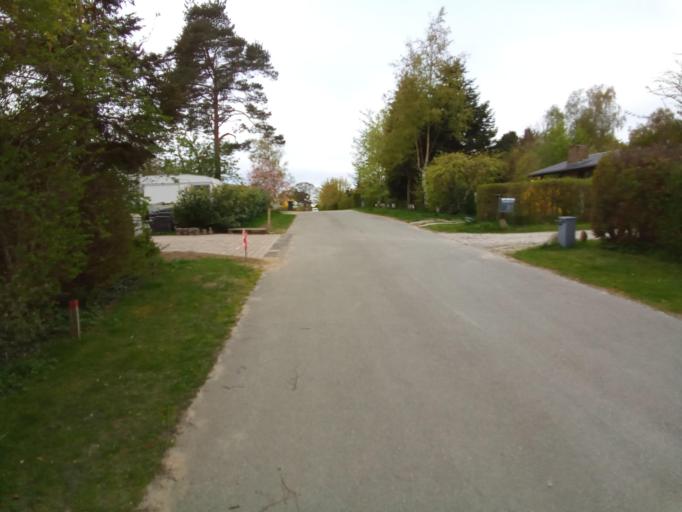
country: DK
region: Capital Region
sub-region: Frederikssund Kommune
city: Frederikssund
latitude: 55.8935
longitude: 12.0612
